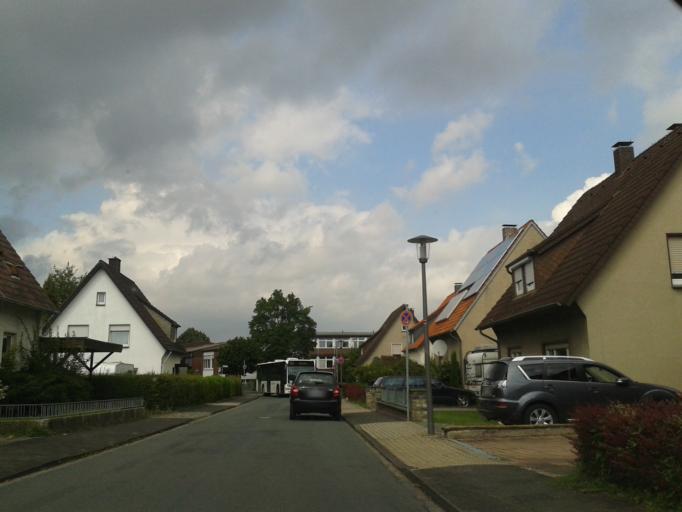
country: DE
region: North Rhine-Westphalia
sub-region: Regierungsbezirk Detmold
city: Lemgo
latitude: 52.0128
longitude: 8.9145
